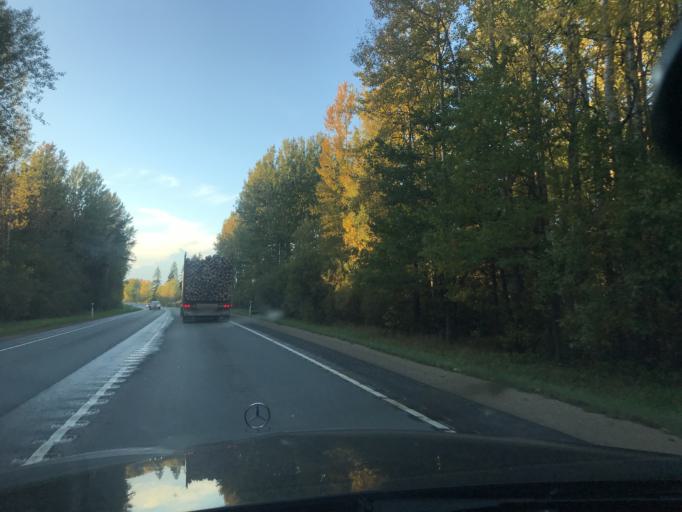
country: EE
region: Vorumaa
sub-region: Voru linn
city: Voru
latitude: 57.8632
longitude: 26.9648
